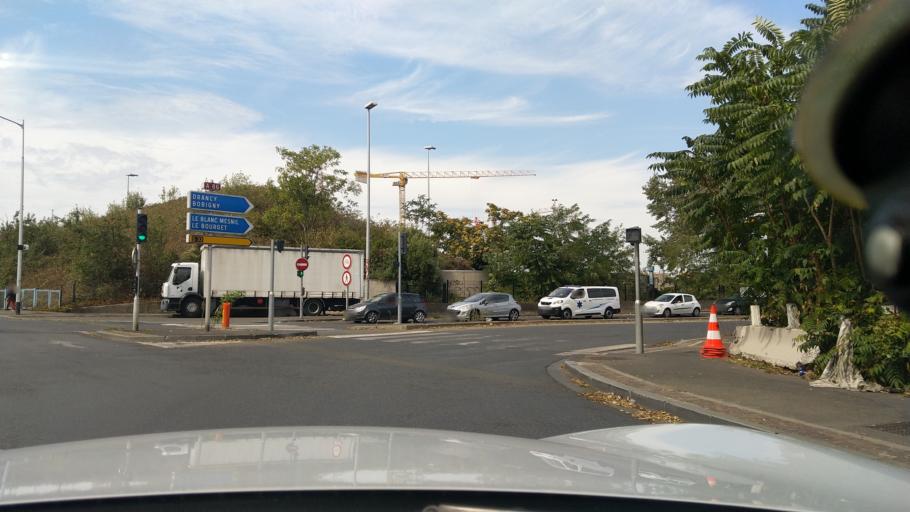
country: FR
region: Ile-de-France
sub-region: Departement de Seine-Saint-Denis
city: La Courneuve
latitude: 48.9251
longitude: 2.4004
